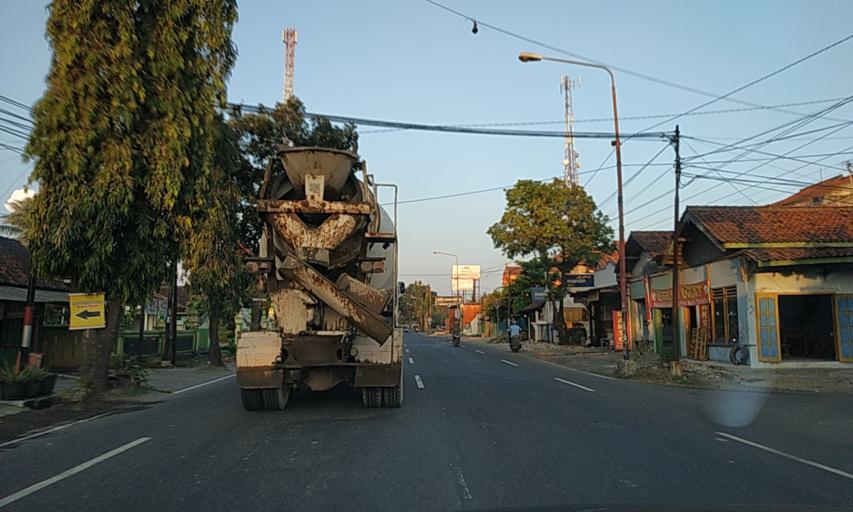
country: ID
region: Daerah Istimewa Yogyakarta
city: Srandakan
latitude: -7.8869
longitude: 110.0774
